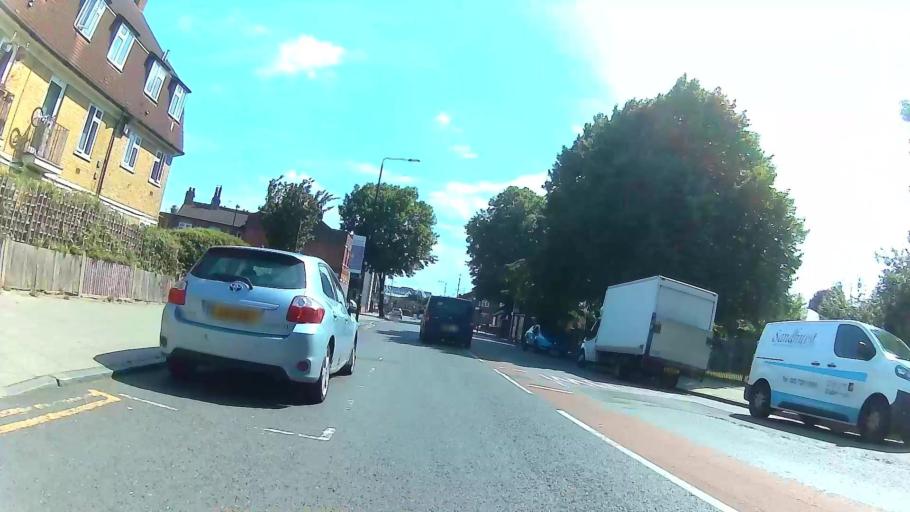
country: GB
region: England
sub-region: Greater London
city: East Ham
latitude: 51.5157
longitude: 0.0319
